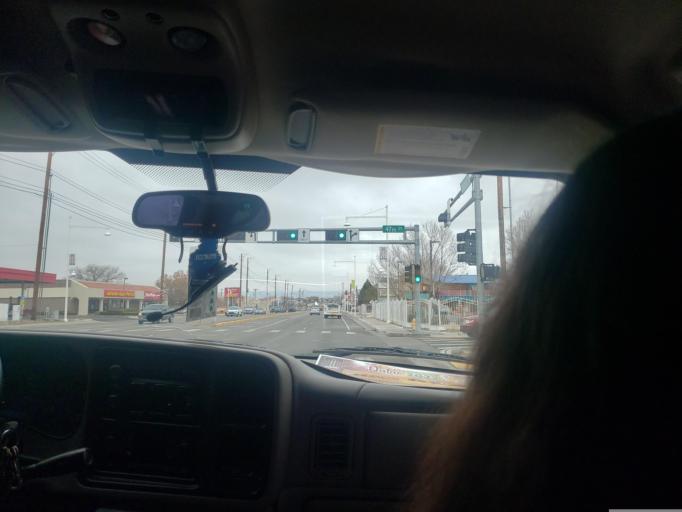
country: US
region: New Mexico
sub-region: Bernalillo County
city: Albuquerque
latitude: 35.0842
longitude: -106.6911
